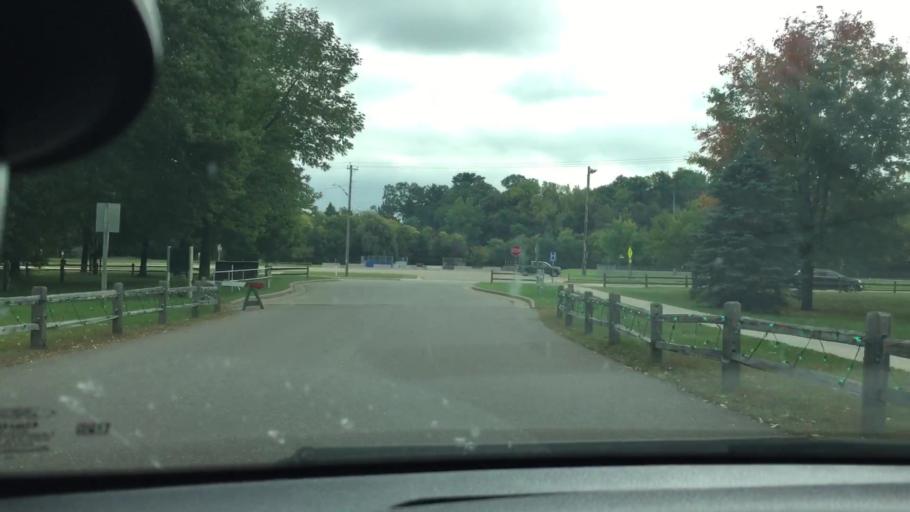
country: US
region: Wisconsin
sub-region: Chippewa County
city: Chippewa Falls
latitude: 44.9451
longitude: -91.4004
